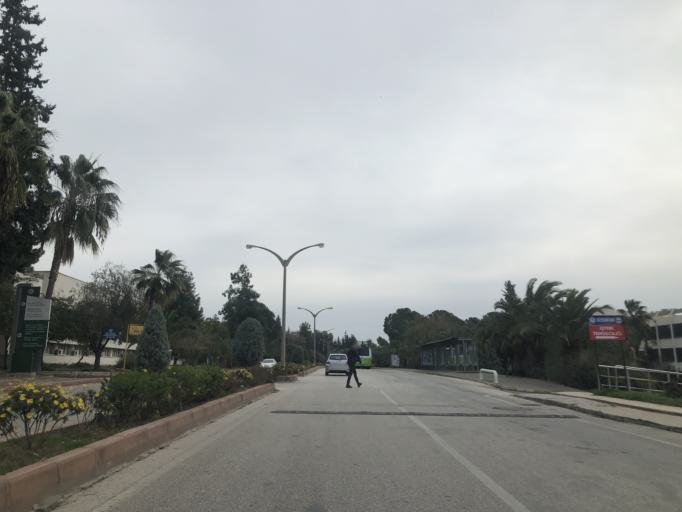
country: TR
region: Adana
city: Adana
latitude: 37.0573
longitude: 35.3570
